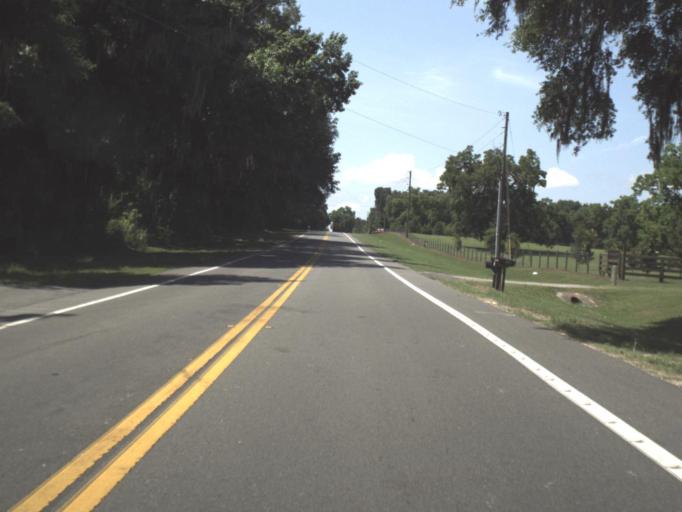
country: US
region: Florida
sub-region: Alachua County
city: Archer
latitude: 29.5224
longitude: -82.4064
